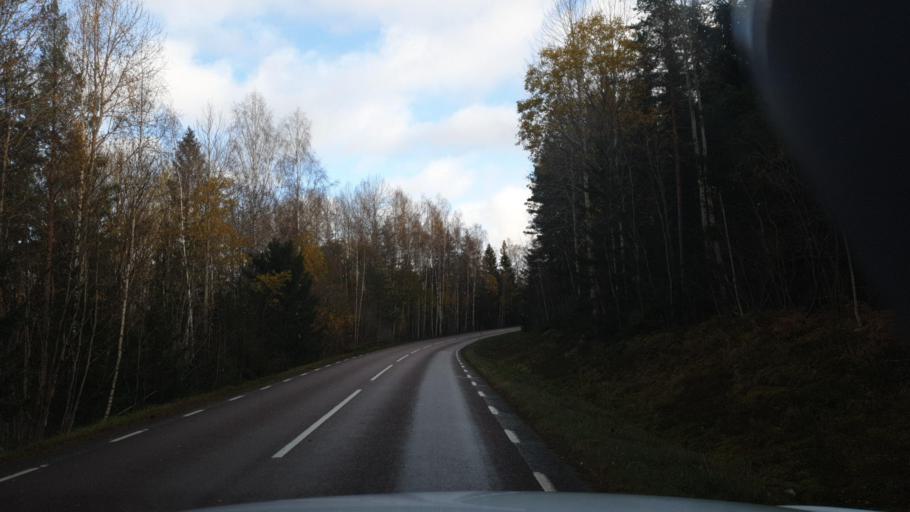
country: SE
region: Vaermland
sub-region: Grums Kommun
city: Grums
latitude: 59.4594
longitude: 12.9380
